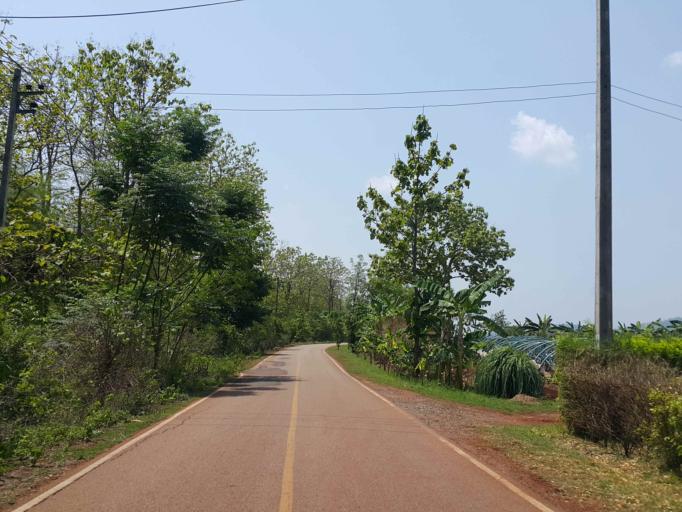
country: TH
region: Chiang Mai
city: Mae Taeng
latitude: 19.0890
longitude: 99.0869
